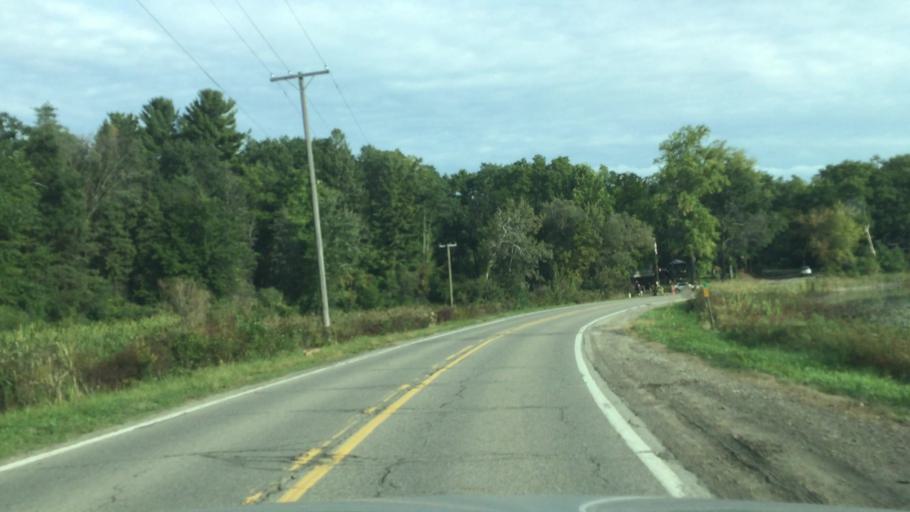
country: US
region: Michigan
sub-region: Livingston County
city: Brighton
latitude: 42.4754
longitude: -83.8357
